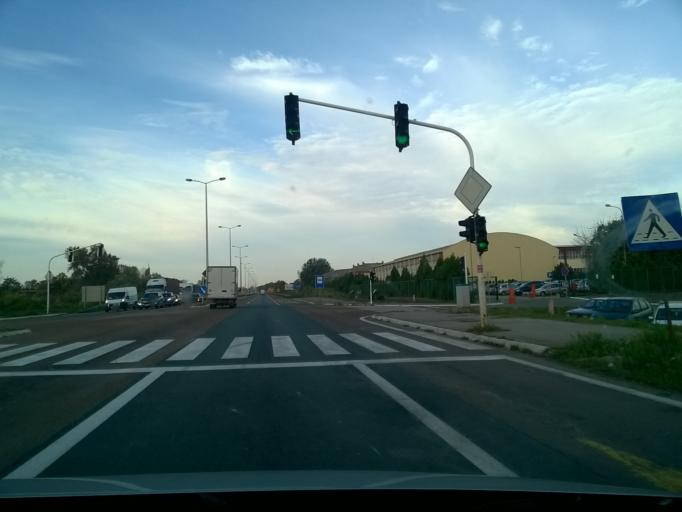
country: RS
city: Ovca
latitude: 44.8500
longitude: 20.5273
